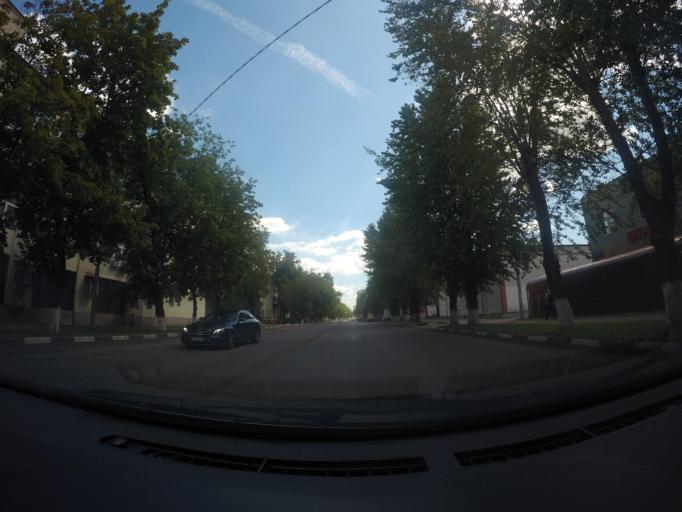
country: RU
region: Moskovskaya
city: Lyubertsy
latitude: 55.6835
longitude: 37.8763
